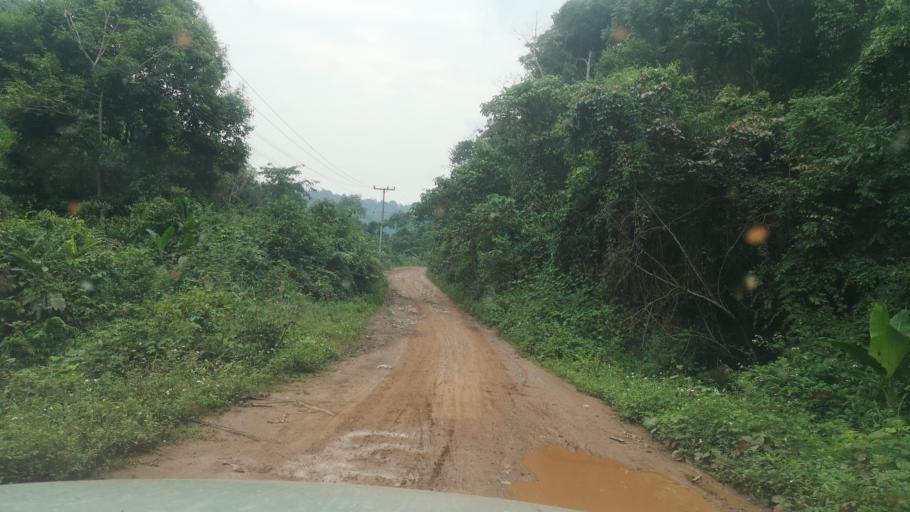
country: LA
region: Oudomxai
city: Muang La
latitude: 21.0751
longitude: 101.8453
